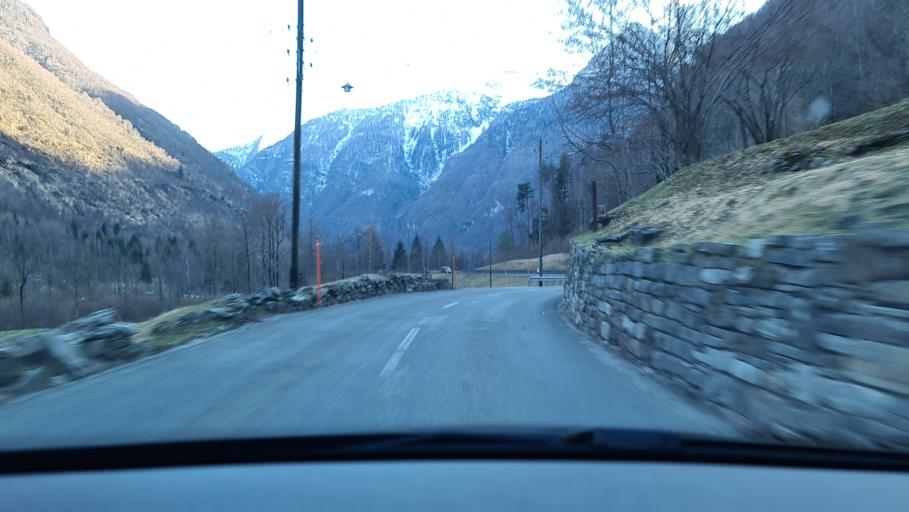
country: CH
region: Ticino
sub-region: Locarno District
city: Lavertezzo
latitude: 46.3099
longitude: 8.7979
